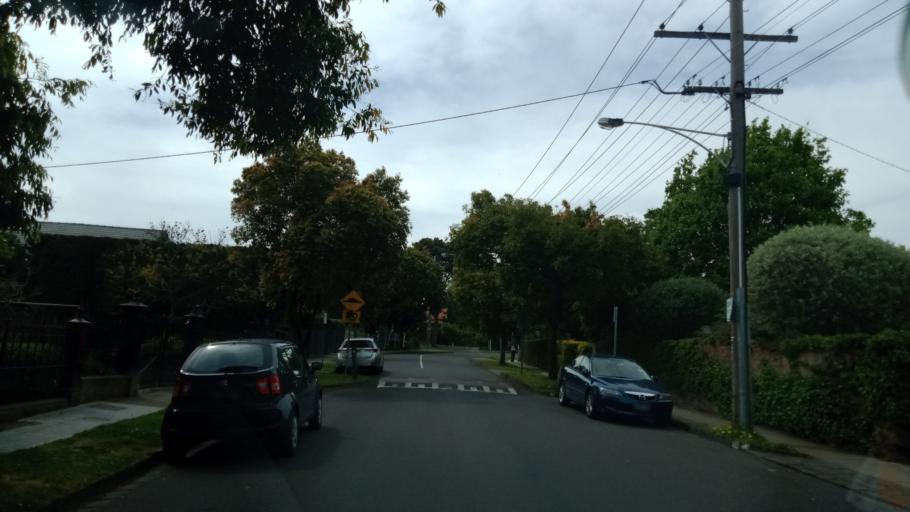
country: AU
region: Victoria
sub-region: Boroondara
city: Hawthorn East
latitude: -37.8266
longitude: 145.0302
